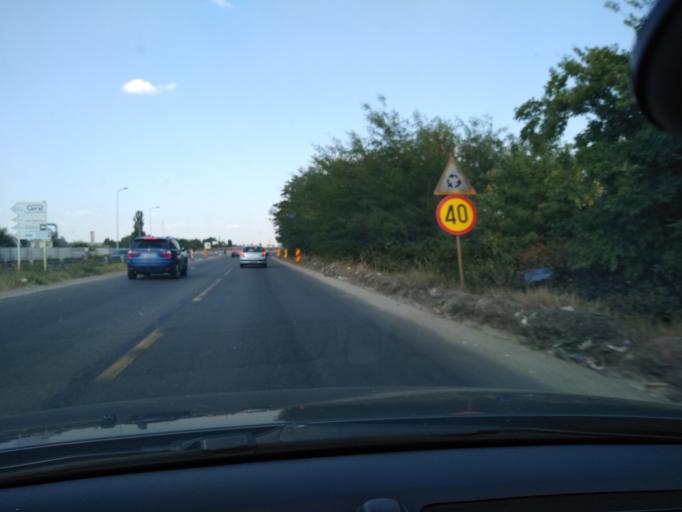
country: RO
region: Ilfov
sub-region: Comuna Chitila
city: Chitila
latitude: 44.4915
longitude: 25.9864
